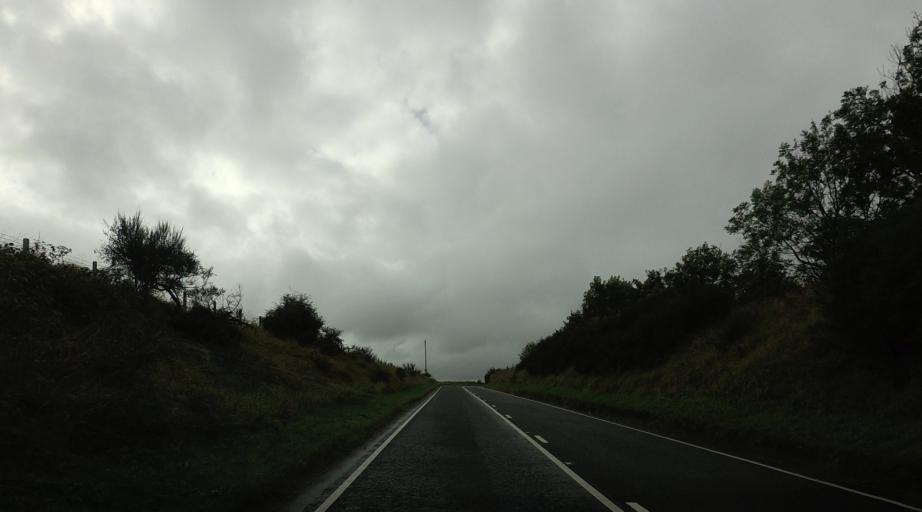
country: GB
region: Scotland
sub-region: Fife
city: Balmullo
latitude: 56.3877
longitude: -2.9121
